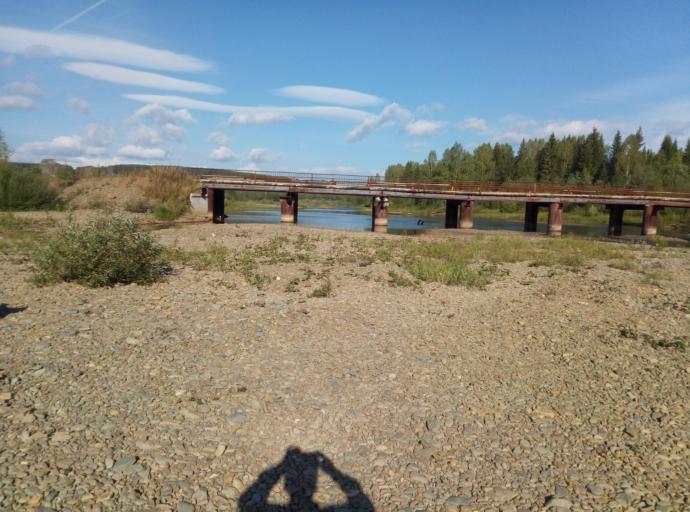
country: RU
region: Sverdlovsk
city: Karpinsk
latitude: 59.4983
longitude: 59.7600
